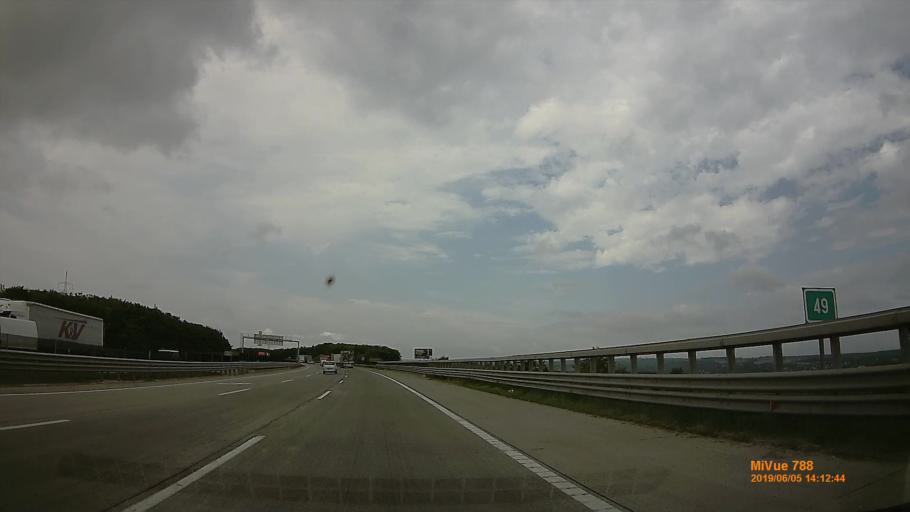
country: HU
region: Pest
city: Pecel
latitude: 47.4713
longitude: 19.3296
